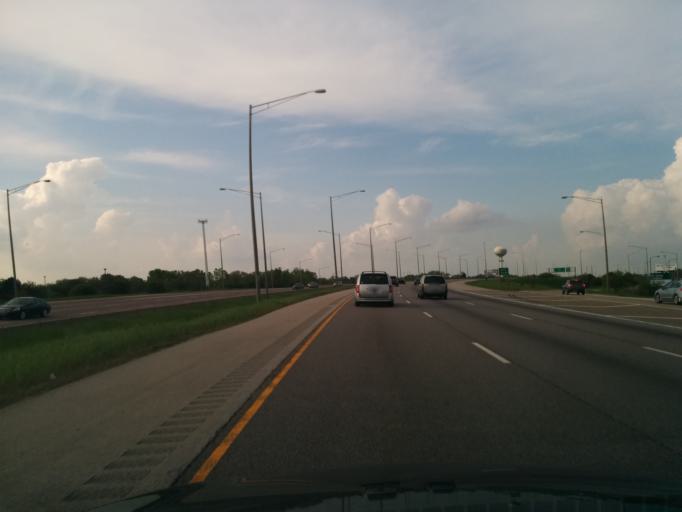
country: US
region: Illinois
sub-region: DuPage County
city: Itasca
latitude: 41.9476
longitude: -88.0372
